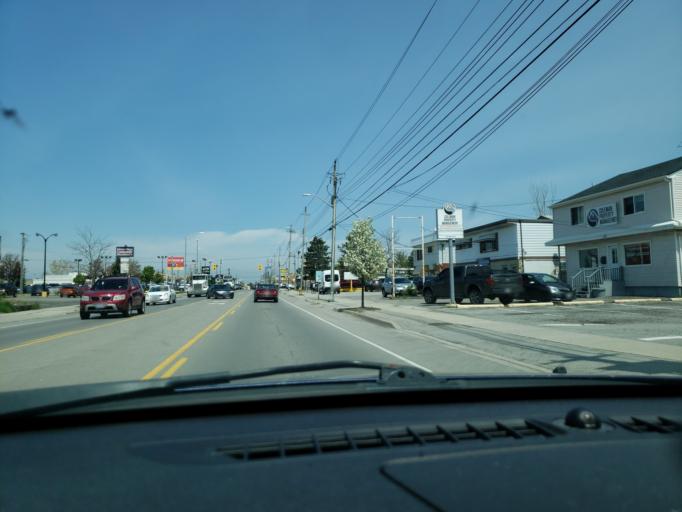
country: CA
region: Ontario
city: Thorold
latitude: 43.1454
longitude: -79.2141
